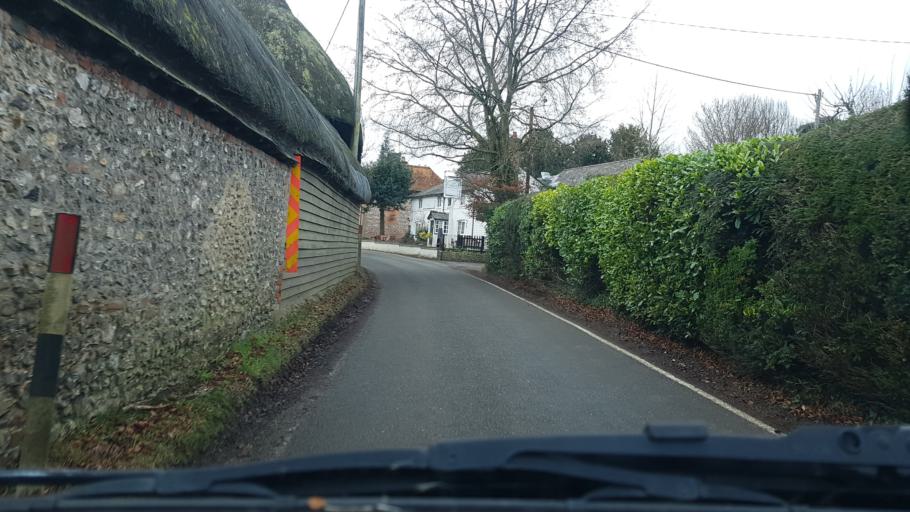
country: GB
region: England
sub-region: Hampshire
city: Andover
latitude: 51.2946
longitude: -1.4855
